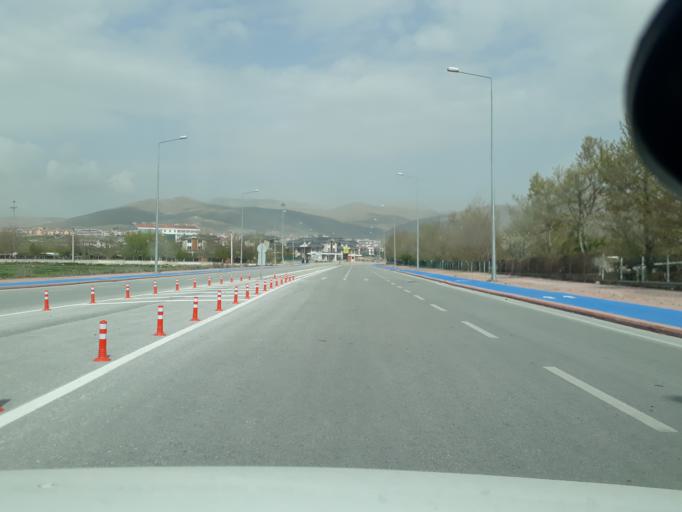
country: TR
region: Konya
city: Sille
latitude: 37.9477
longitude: 32.4779
